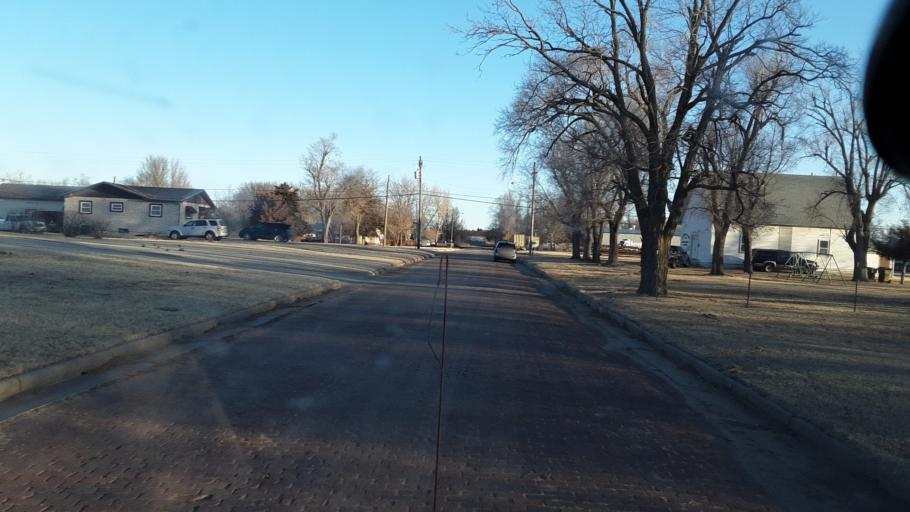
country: US
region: Kansas
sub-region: Rice County
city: Lyons
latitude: 38.3543
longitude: -98.2032
